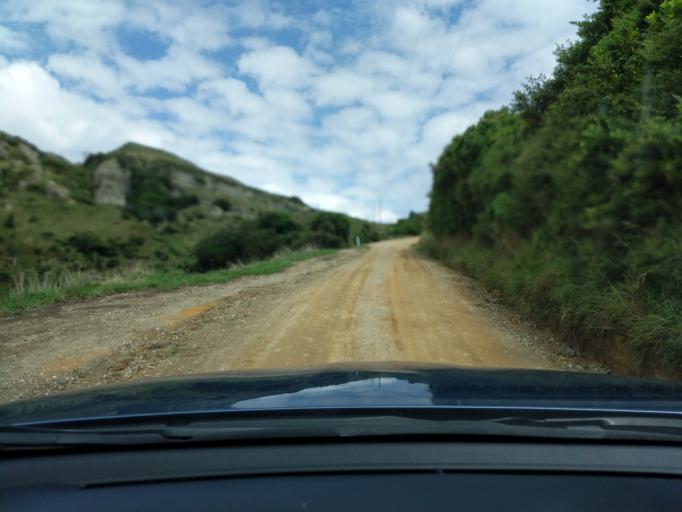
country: NZ
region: Tasman
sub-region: Tasman District
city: Takaka
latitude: -40.6576
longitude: 172.4168
